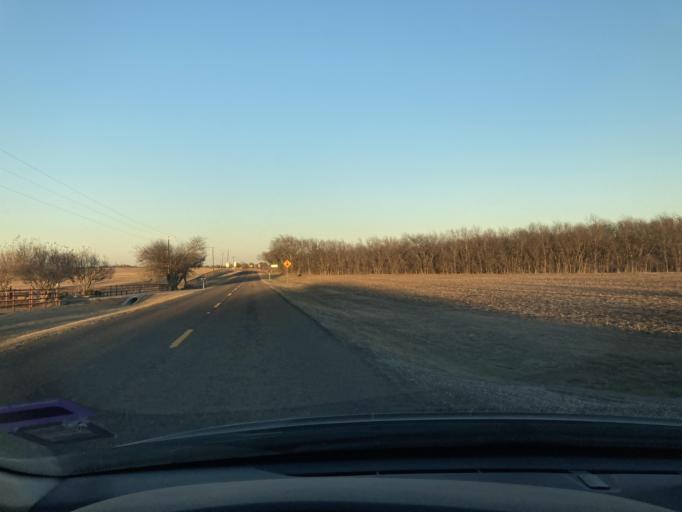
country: US
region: Texas
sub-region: Ellis County
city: Waxahachie
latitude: 32.3425
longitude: -96.8772
